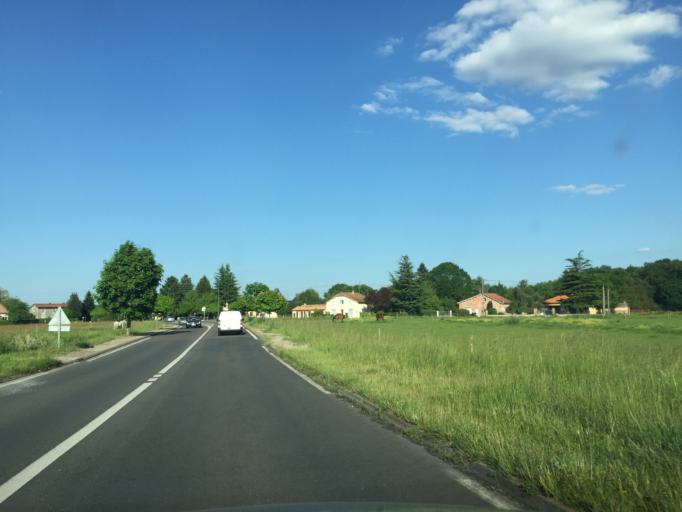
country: FR
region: Aquitaine
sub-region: Departement de la Gironde
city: Les Eglisottes-et-Chalaures
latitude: 45.0899
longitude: -0.0489
